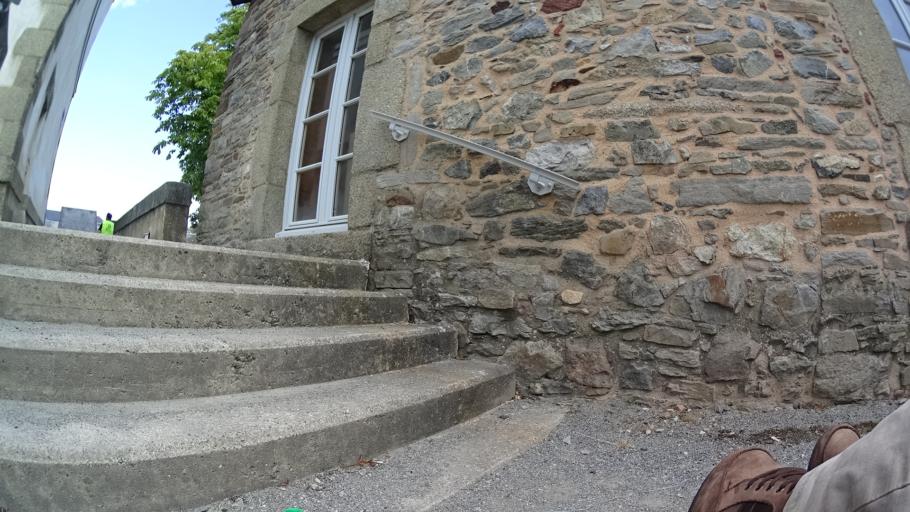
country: FR
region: Brittany
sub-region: Departement d'Ille-et-Vilaine
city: Redon
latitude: 47.6508
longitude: -2.0897
